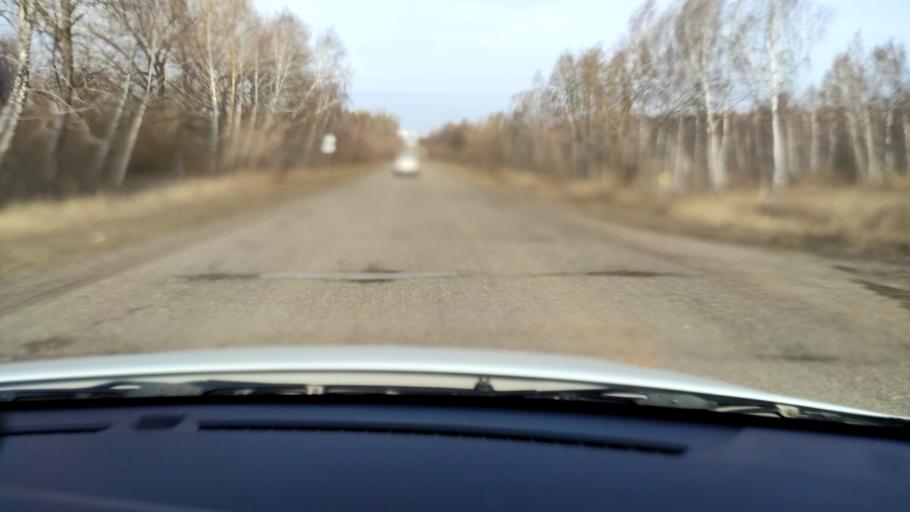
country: RU
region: Tatarstan
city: Stolbishchi
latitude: 55.7201
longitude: 49.2121
